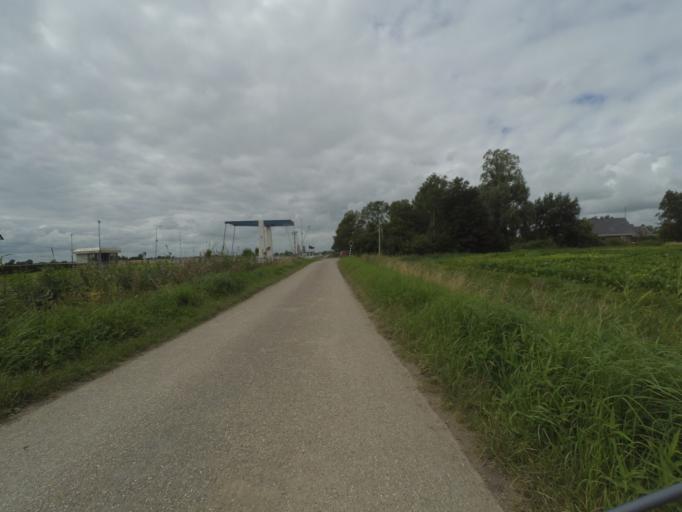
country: NL
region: Friesland
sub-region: Gemeente Kollumerland en Nieuwkruisland
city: Kollum
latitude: 53.3164
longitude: 6.1403
